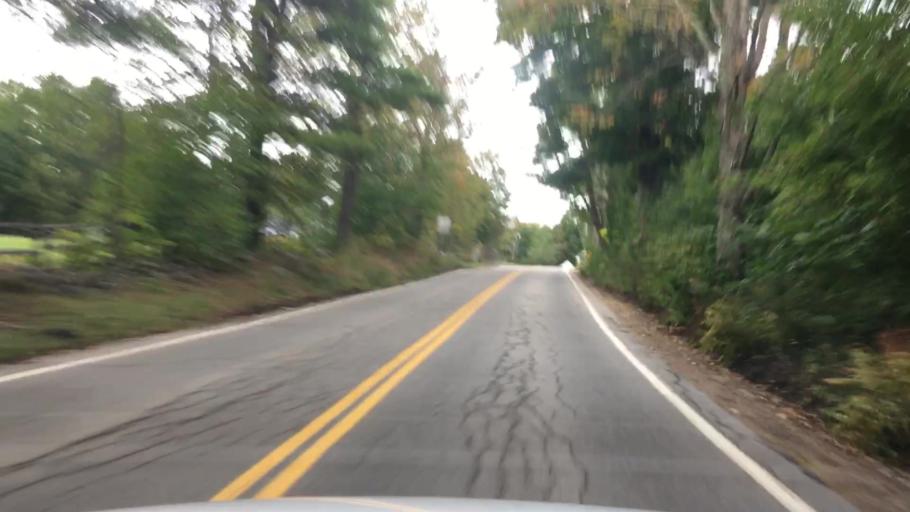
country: US
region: New Hampshire
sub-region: Carroll County
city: Effingham
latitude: 43.7598
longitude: -70.9980
